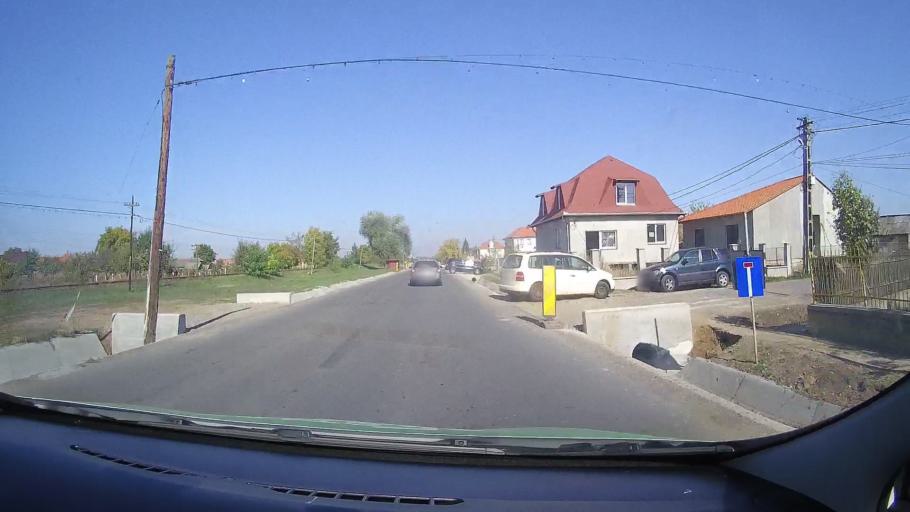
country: RO
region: Satu Mare
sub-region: Comuna Berveni
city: Lucaceni
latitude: 47.7400
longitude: 22.4747
